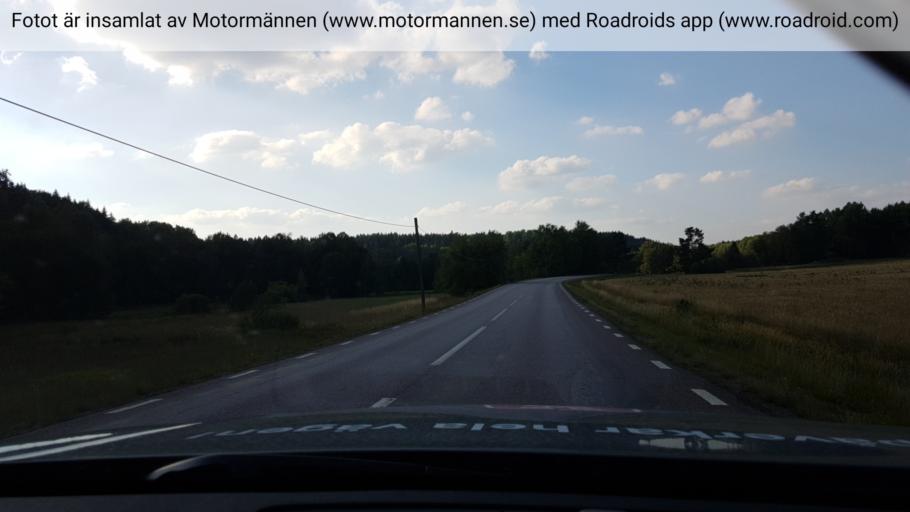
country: SE
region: Soedermanland
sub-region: Strangnas Kommun
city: Mariefred
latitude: 59.2218
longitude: 17.1659
